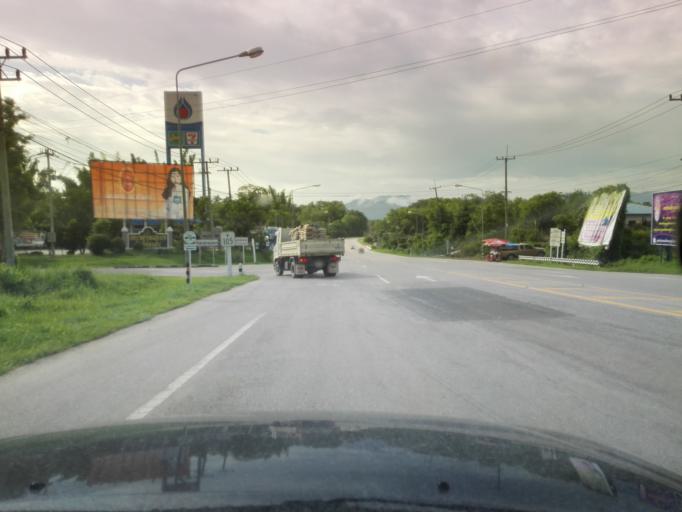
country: TH
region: Tak
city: Mae Ramat
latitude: 16.9771
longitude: 98.5285
